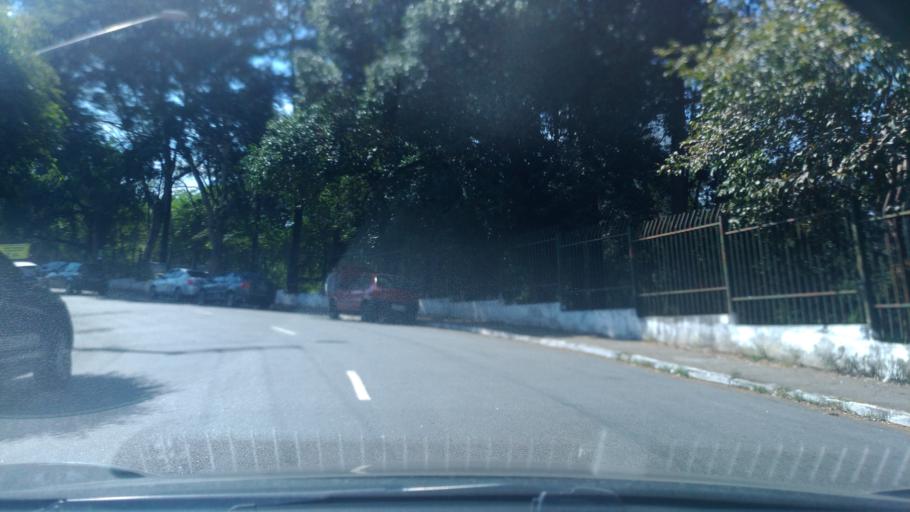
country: BR
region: Sao Paulo
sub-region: Sao Paulo
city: Sao Paulo
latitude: -23.5699
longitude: -46.5897
